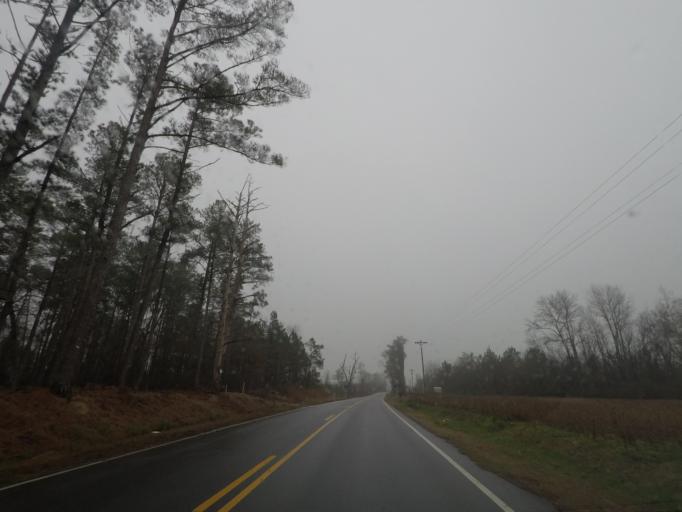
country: US
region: North Carolina
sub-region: Scotland County
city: Laurinburg
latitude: 34.8107
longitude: -79.4460
